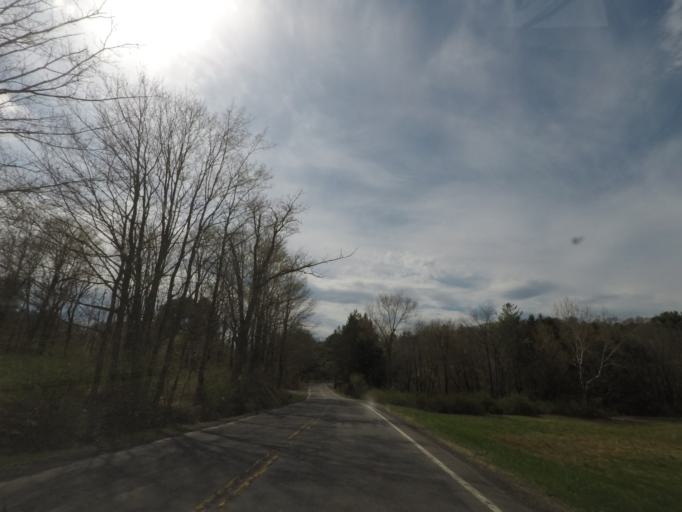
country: US
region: New York
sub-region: Columbia County
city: Chatham
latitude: 42.3452
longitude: -73.5839
